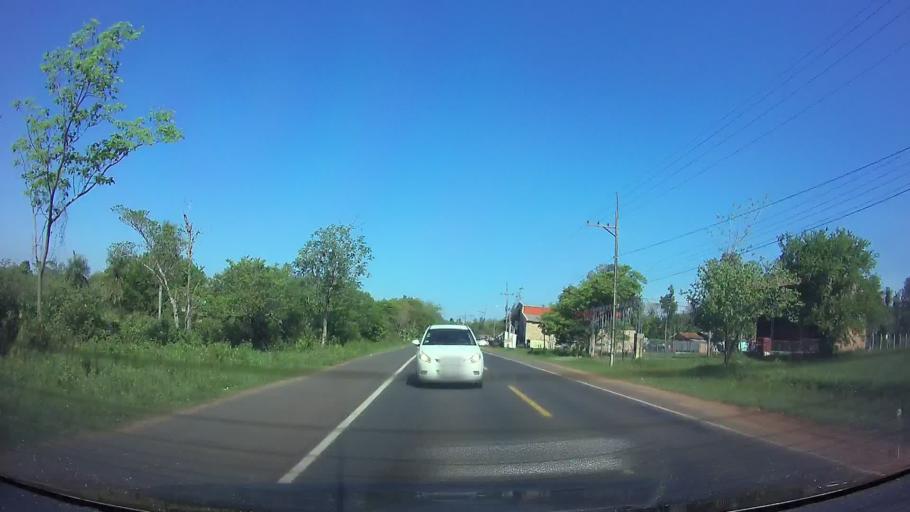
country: PY
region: Central
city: Itaugua
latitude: -25.3682
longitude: -57.3103
